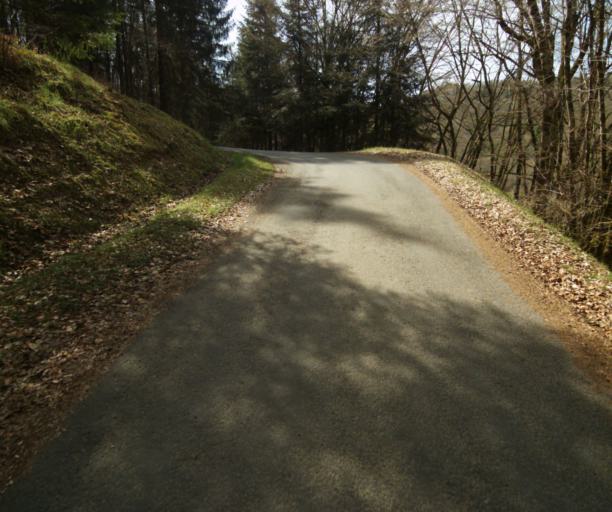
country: FR
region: Limousin
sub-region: Departement de la Correze
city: Naves
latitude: 45.3690
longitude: 1.7887
